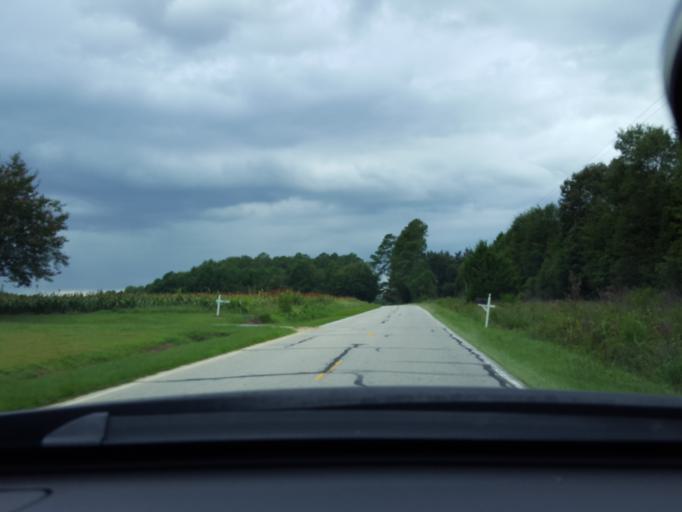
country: US
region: North Carolina
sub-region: Sampson County
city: Clinton
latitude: 34.8001
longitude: -78.2406
